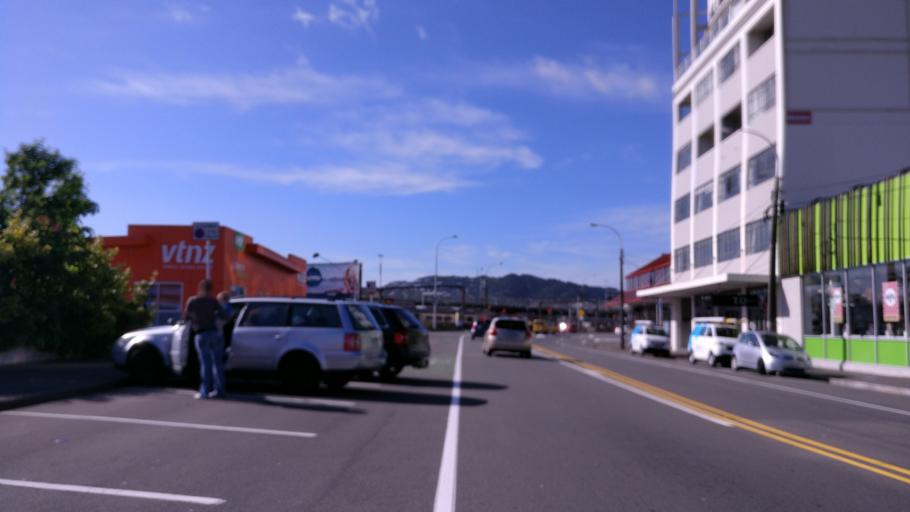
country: NZ
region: Wellington
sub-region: Wellington City
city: Wellington
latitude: -41.2738
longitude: 174.7832
